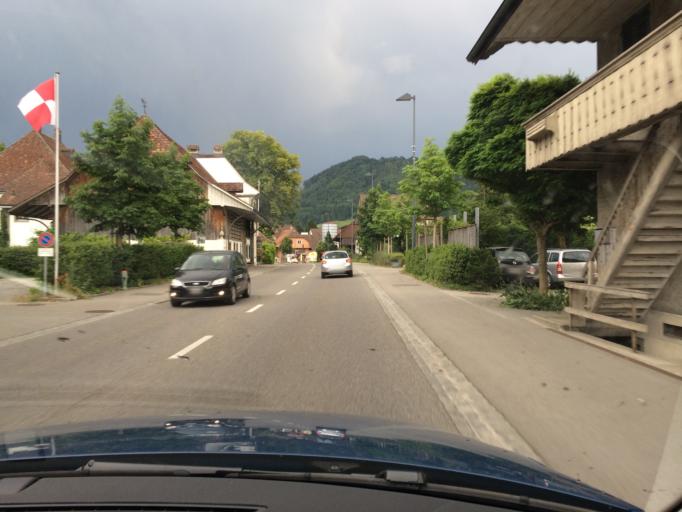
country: CH
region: Bern
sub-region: Bern-Mittelland District
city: Belp
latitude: 46.8929
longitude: 7.5011
